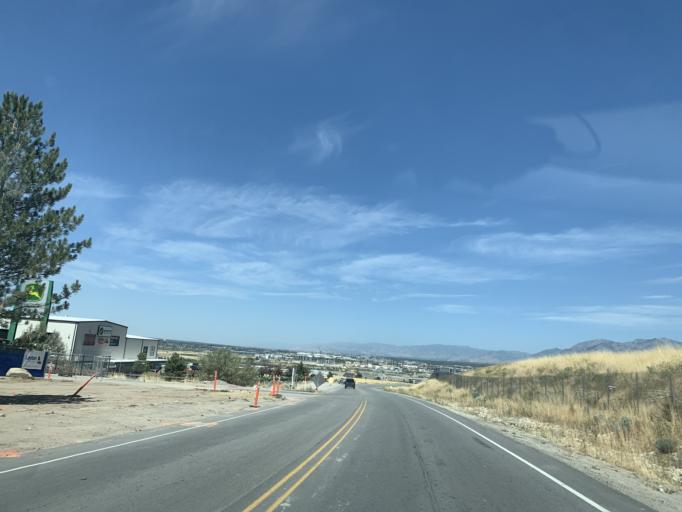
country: US
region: Utah
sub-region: Salt Lake County
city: Bluffdale
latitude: 40.4815
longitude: -111.9028
